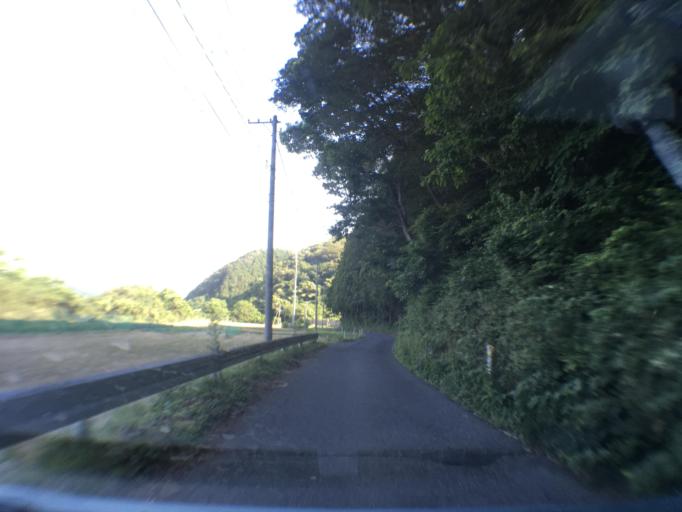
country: JP
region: Miyagi
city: Wakuya
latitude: 38.6364
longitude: 141.2841
